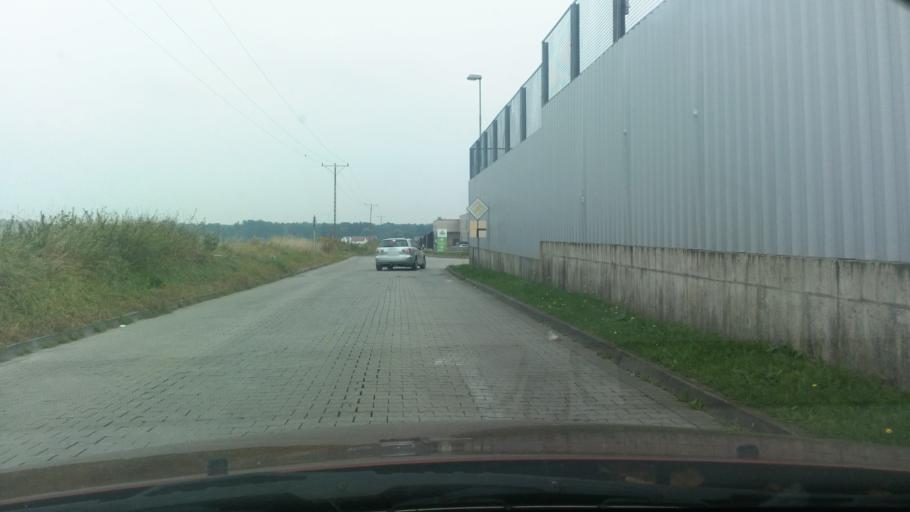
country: PL
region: Lower Silesian Voivodeship
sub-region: Powiat zgorzelecki
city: Lagow
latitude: 51.1571
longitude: 15.0311
